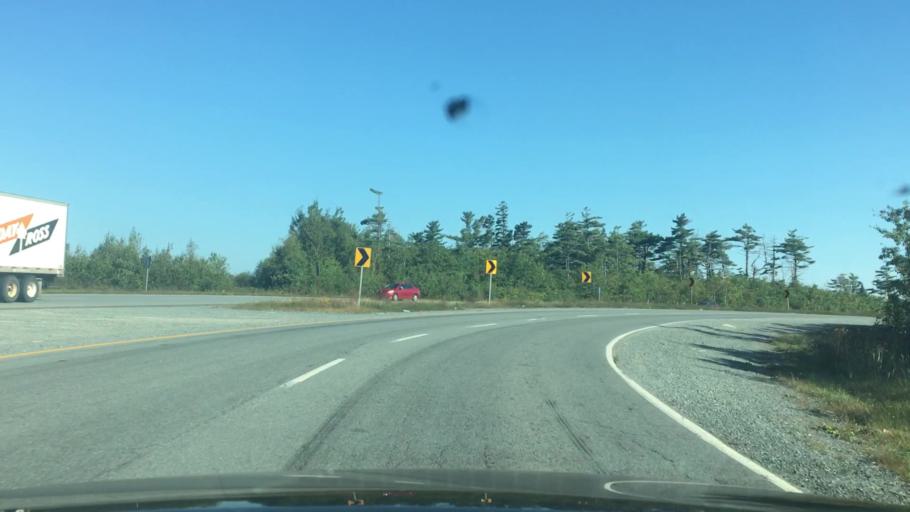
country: CA
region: Nova Scotia
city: Dartmouth
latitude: 44.7209
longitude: -63.5809
